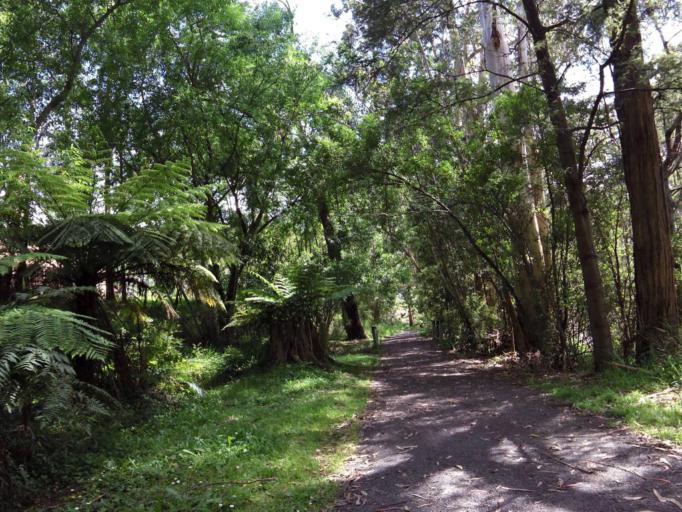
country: AU
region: Victoria
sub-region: Yarra Ranges
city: Millgrove
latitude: -37.7516
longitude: 145.6986
